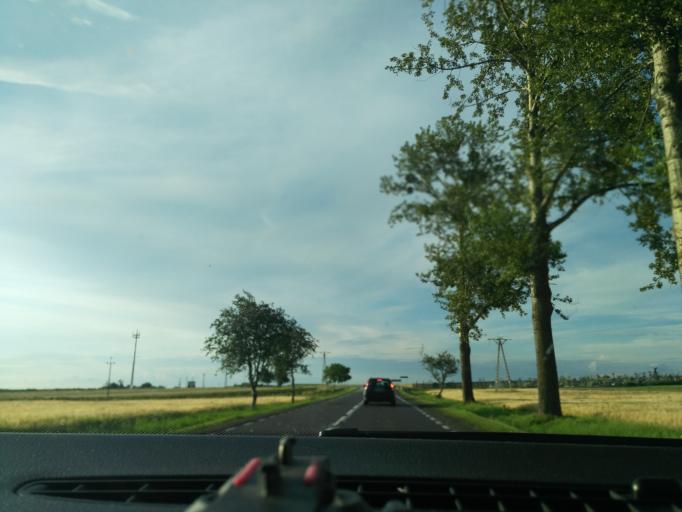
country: PL
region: Lublin Voivodeship
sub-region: Powiat krasnicki
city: Szastarka
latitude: 50.8145
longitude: 22.3192
